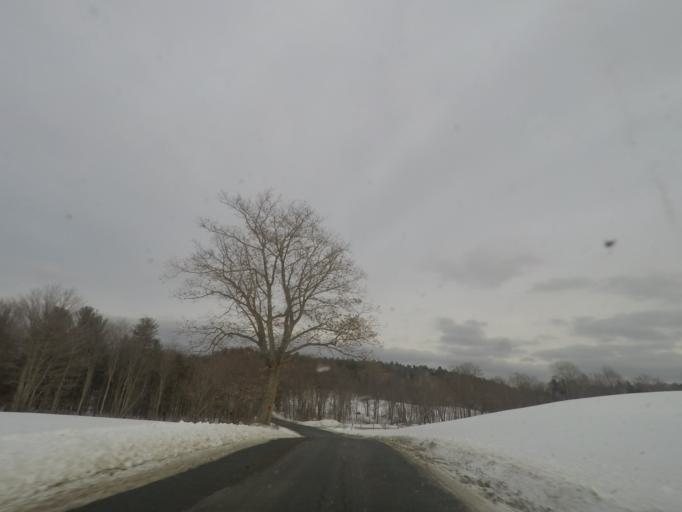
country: US
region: New York
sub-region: Rensselaer County
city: Averill Park
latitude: 42.5813
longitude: -73.5736
